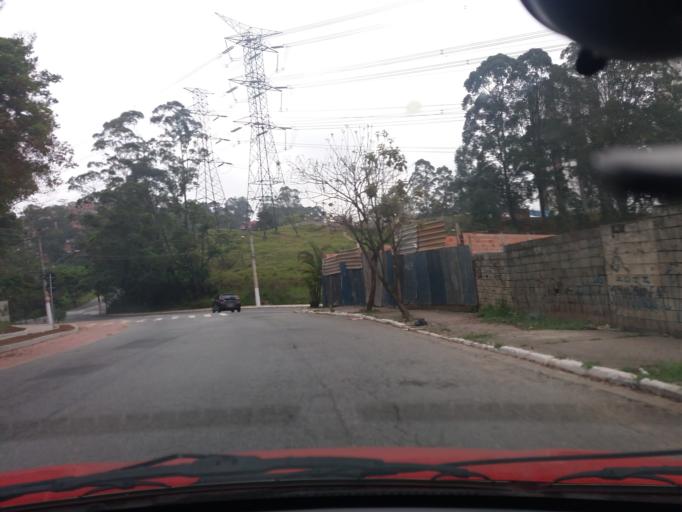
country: BR
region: Sao Paulo
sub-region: Taboao Da Serra
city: Taboao da Serra
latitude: -23.6273
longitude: -46.7442
